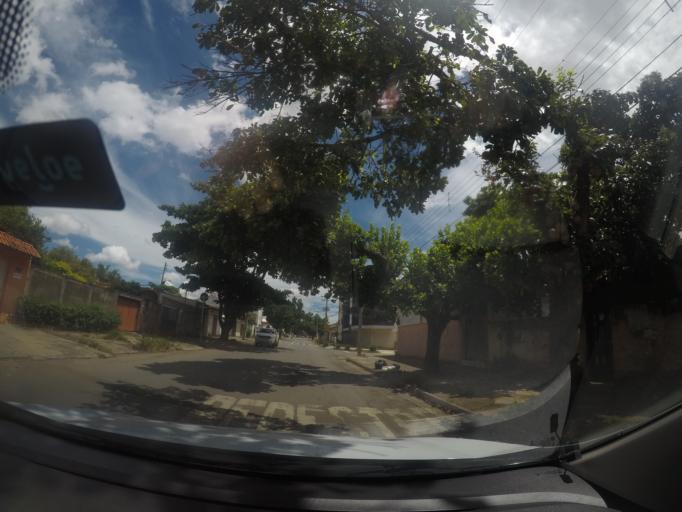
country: BR
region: Goias
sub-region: Goiania
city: Goiania
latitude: -16.6781
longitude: -49.3169
